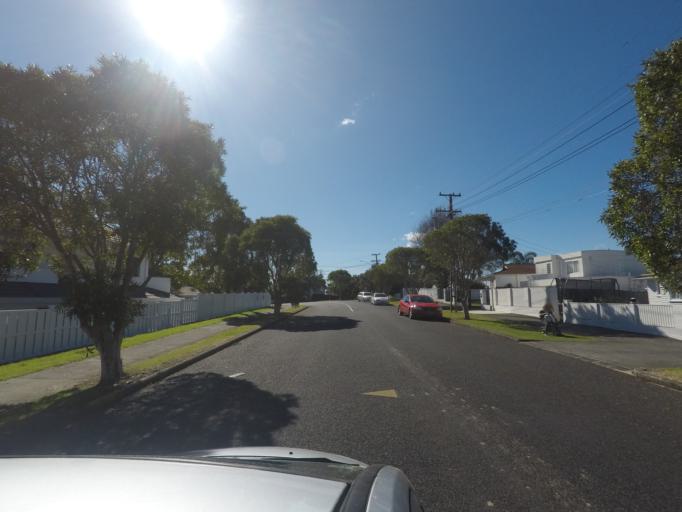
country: NZ
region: Auckland
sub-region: Auckland
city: Waitakere
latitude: -36.9300
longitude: 174.6975
